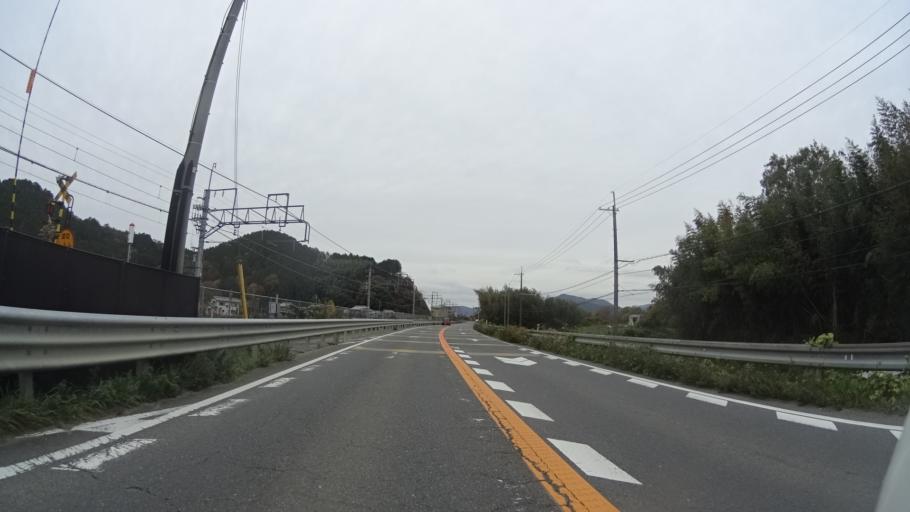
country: JP
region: Kyoto
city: Kameoka
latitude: 35.0640
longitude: 135.5425
